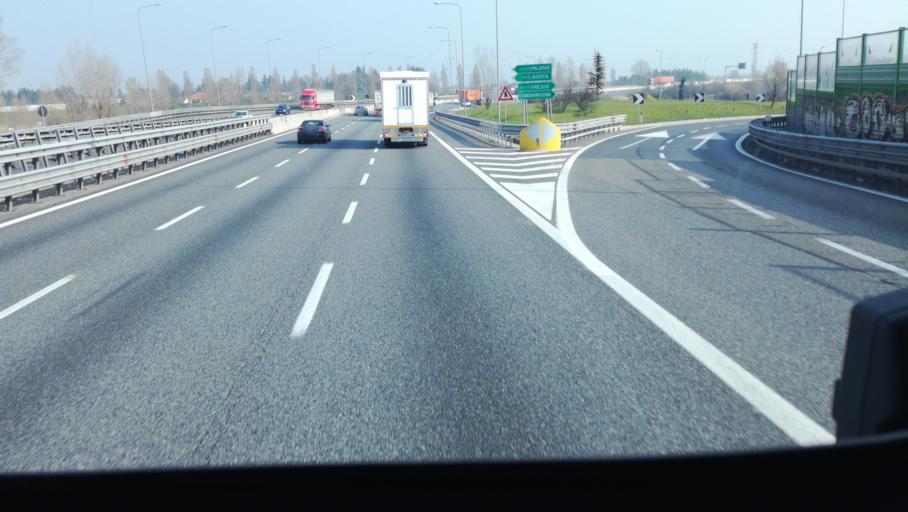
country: IT
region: Piedmont
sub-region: Provincia di Torino
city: Rivoli
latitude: 45.0784
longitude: 7.5484
